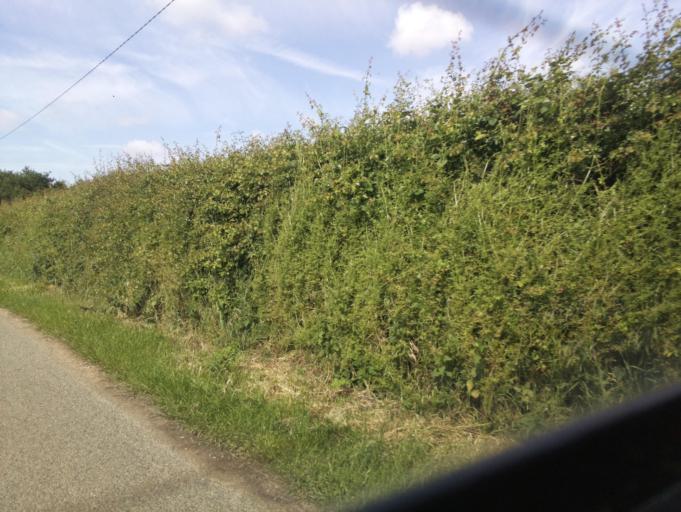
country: GB
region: England
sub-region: Lincolnshire
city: Skellingthorpe
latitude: 53.1504
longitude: -0.6295
